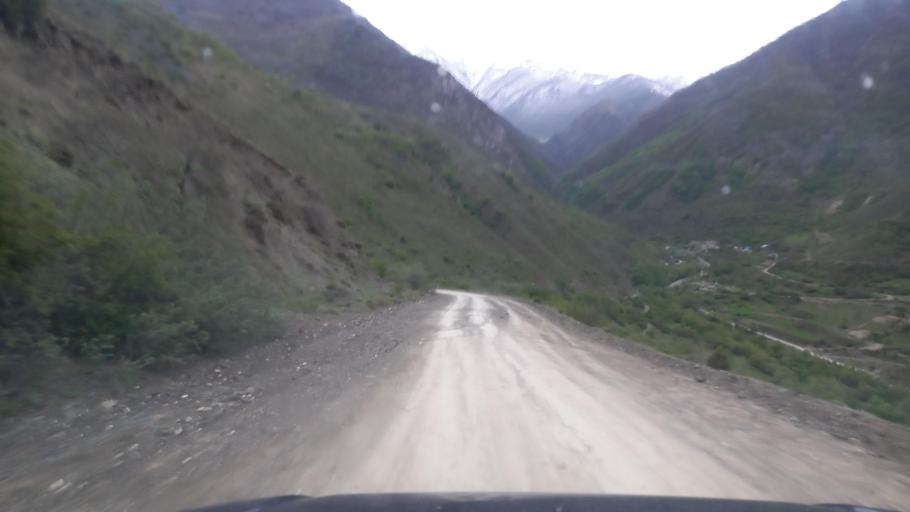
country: RU
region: North Ossetia
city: Mizur
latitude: 42.8559
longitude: 44.1577
